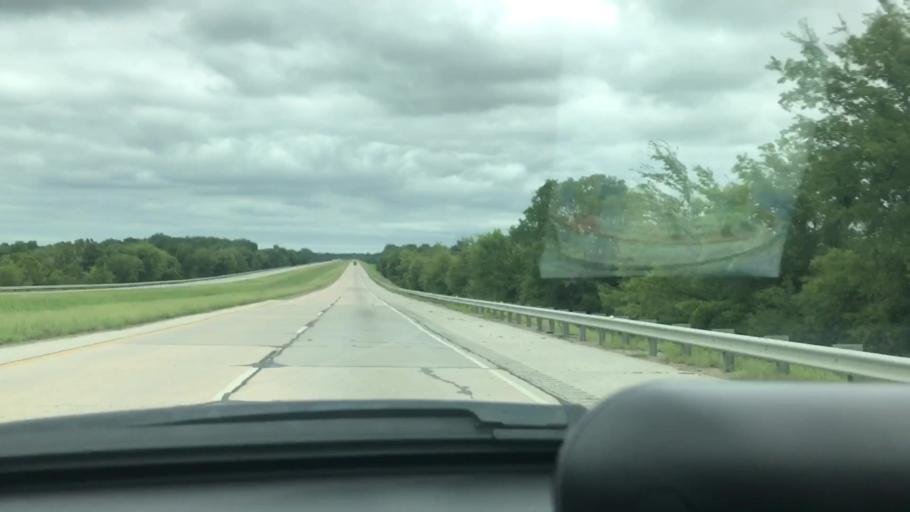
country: US
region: Oklahoma
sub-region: Wagoner County
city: Wagoner
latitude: 35.8897
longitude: -95.4026
